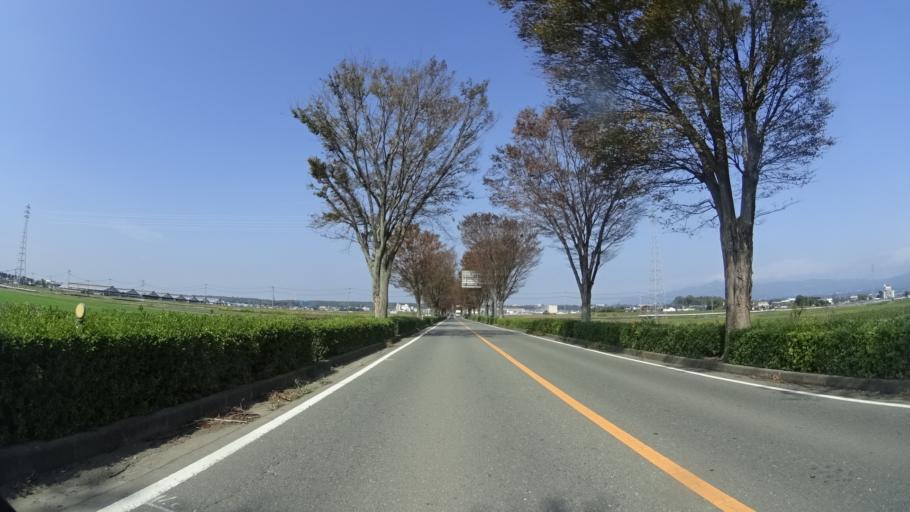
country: JP
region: Kumamoto
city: Ozu
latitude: 32.8598
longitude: 130.8553
